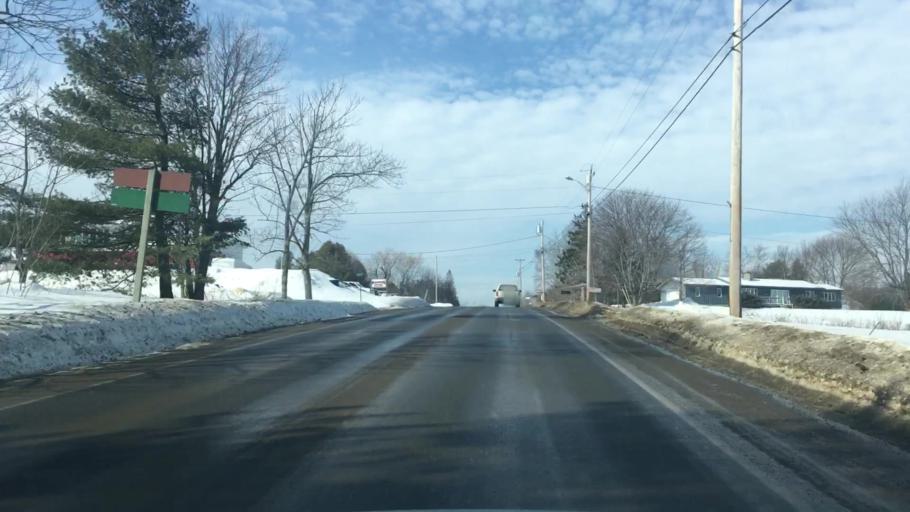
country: US
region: Maine
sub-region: Penobscot County
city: Hermon
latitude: 44.8453
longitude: -68.8680
